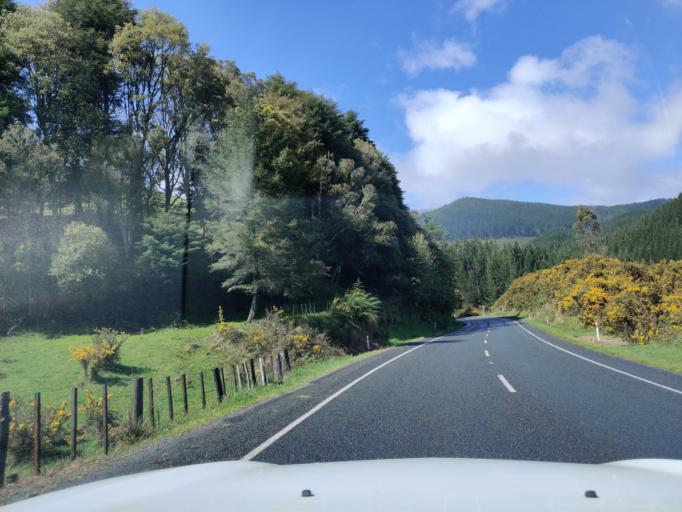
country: NZ
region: Bay of Plenty
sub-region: Rotorua District
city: Rotorua
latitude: -38.1629
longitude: 176.3069
